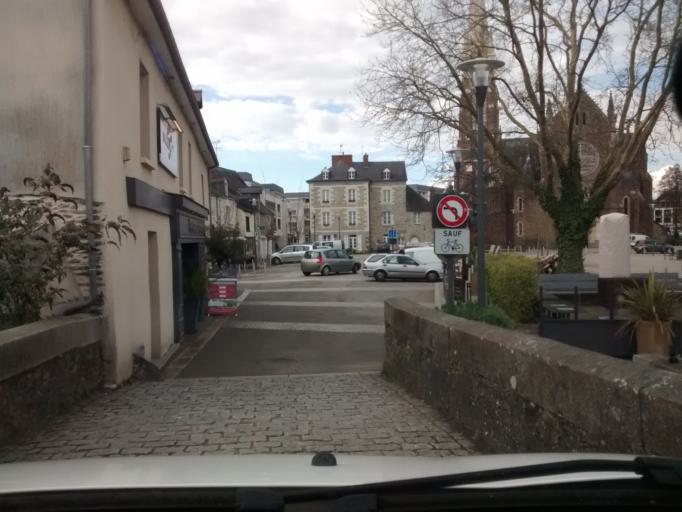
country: FR
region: Brittany
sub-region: Departement d'Ille-et-Vilaine
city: Cesson-Sevigne
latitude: 48.1163
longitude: -1.6044
